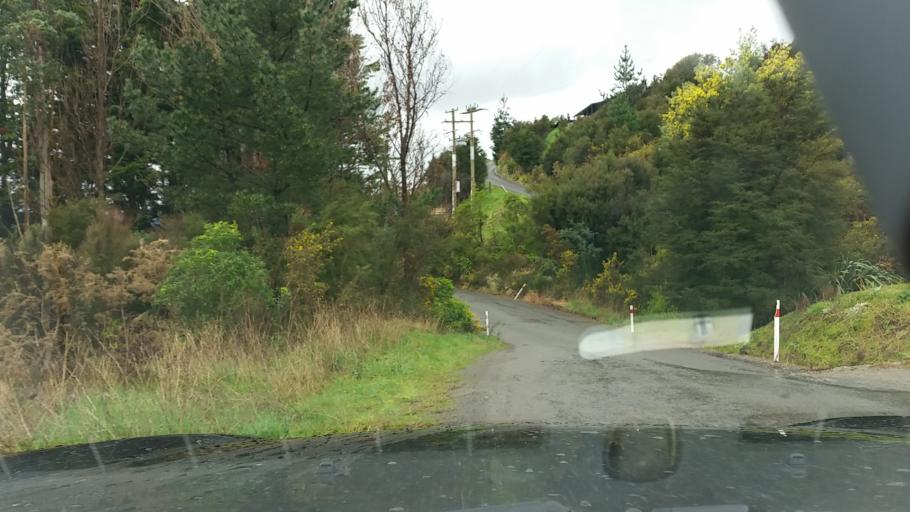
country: NZ
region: Marlborough
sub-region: Marlborough District
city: Picton
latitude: -41.2789
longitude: 174.0323
